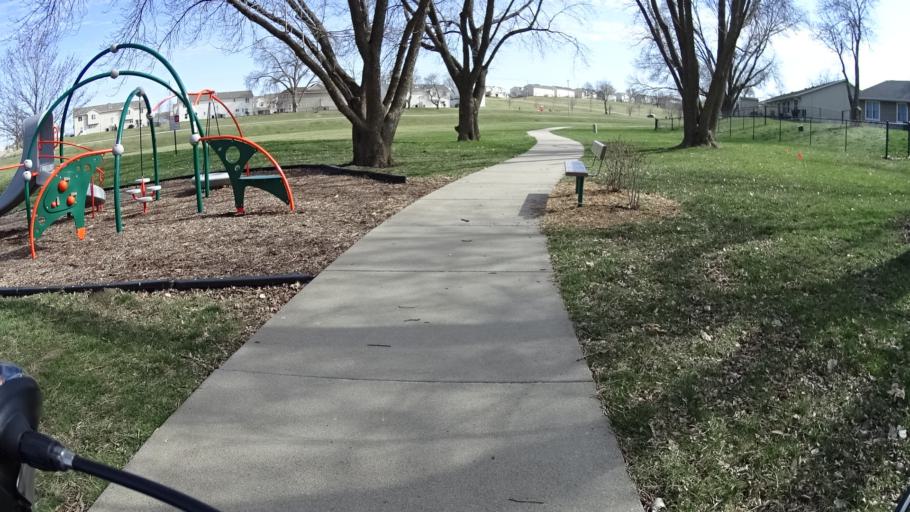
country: US
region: Nebraska
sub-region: Sarpy County
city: Offutt Air Force Base
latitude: 41.1281
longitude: -95.9544
